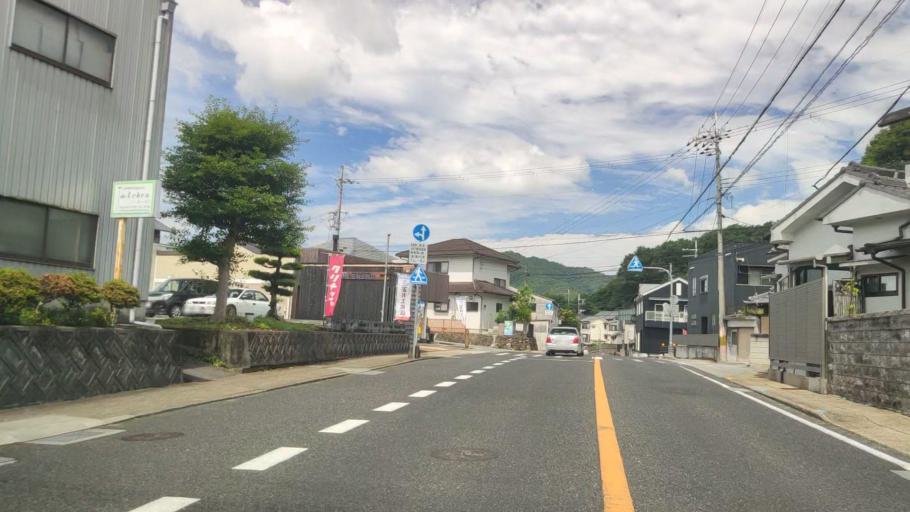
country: JP
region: Hyogo
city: Nishiwaki
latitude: 34.9911
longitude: 134.9763
